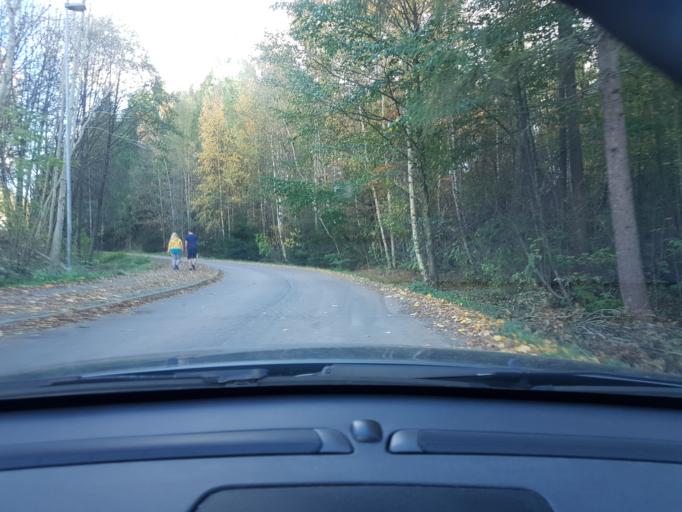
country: SE
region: Vaestra Goetaland
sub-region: Ale Kommun
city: Surte
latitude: 57.8195
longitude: 12.0236
